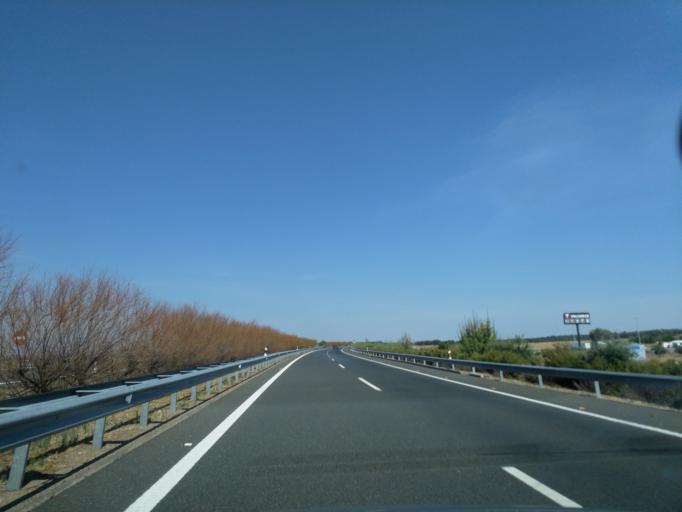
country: ES
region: Extremadura
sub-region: Provincia de Caceres
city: Aldea del Cano
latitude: 39.2873
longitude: -6.3301
